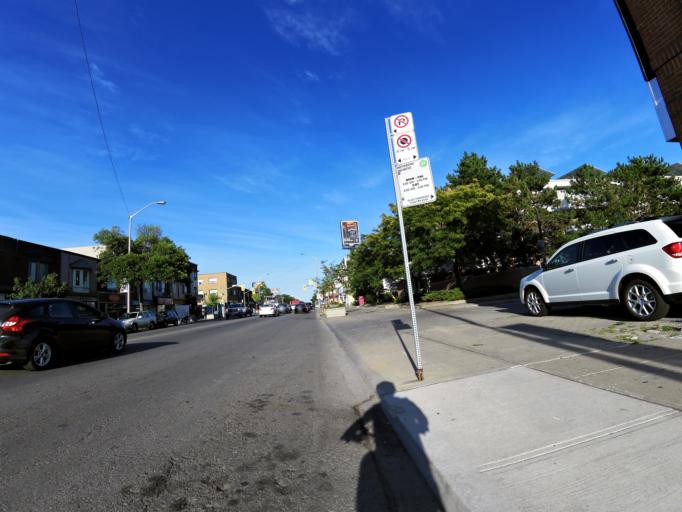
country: CA
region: Ontario
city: Toronto
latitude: 43.6817
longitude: -79.3307
